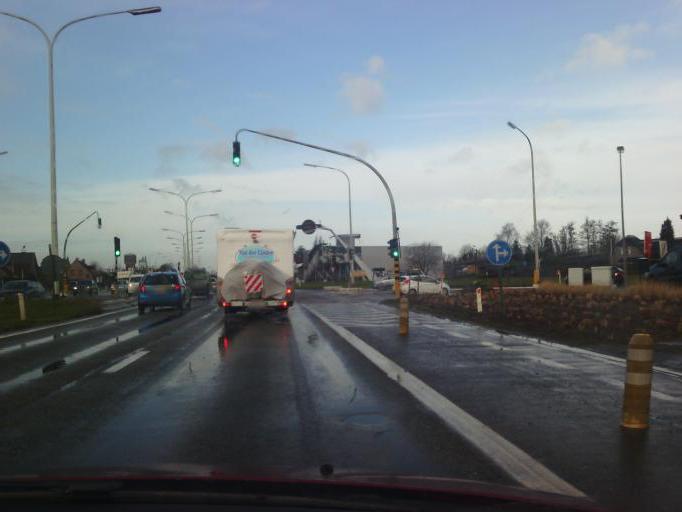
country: BE
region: Flanders
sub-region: Provincie Oost-Vlaanderen
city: Lokeren
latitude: 51.0929
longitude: 4.0154
